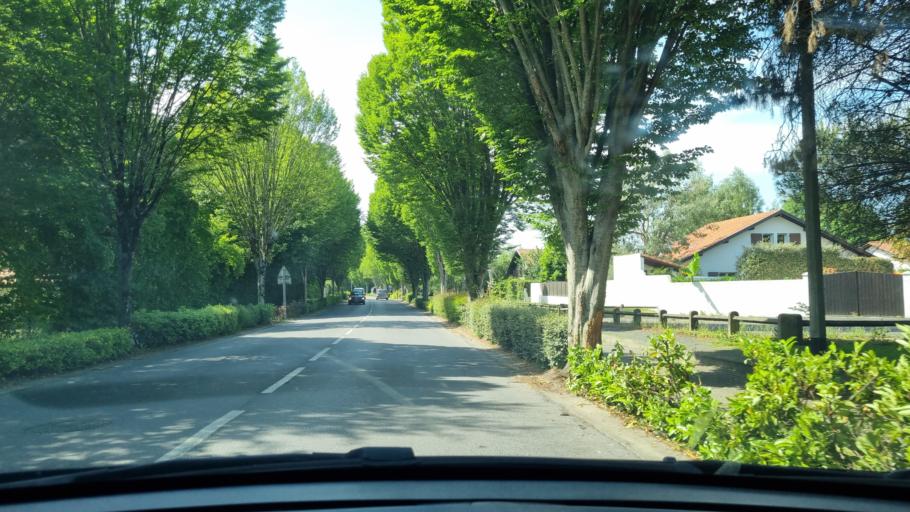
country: FR
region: Aquitaine
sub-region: Departement des Pyrenees-Atlantiques
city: Anglet
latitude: 43.4747
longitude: -1.5007
